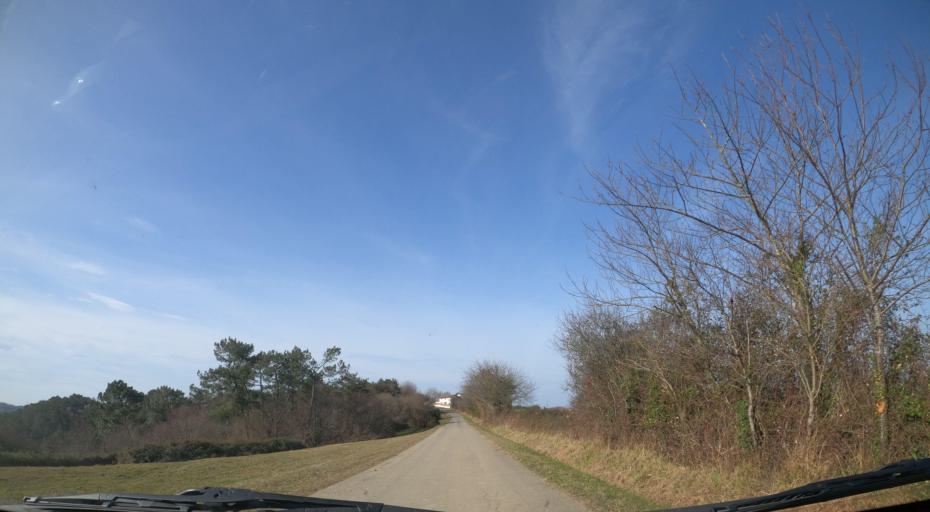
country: FR
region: Aquitaine
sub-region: Departement des Pyrenees-Atlantiques
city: Briscous
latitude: 43.4258
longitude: -1.3709
